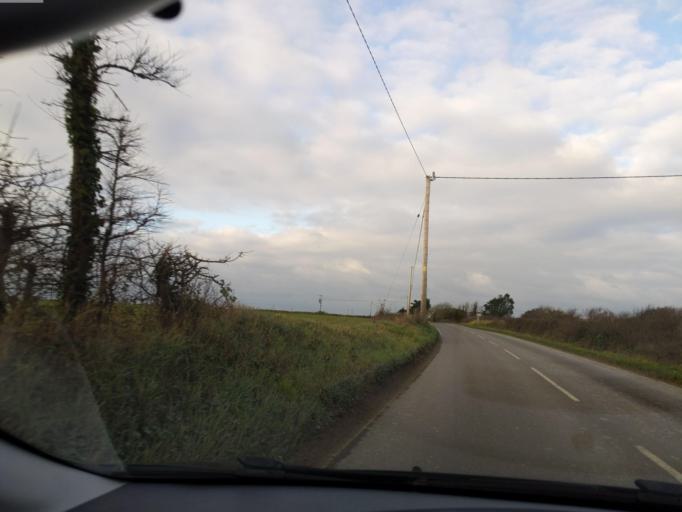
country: GB
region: England
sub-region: Cornwall
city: Padstow
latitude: 50.5224
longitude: -4.9519
